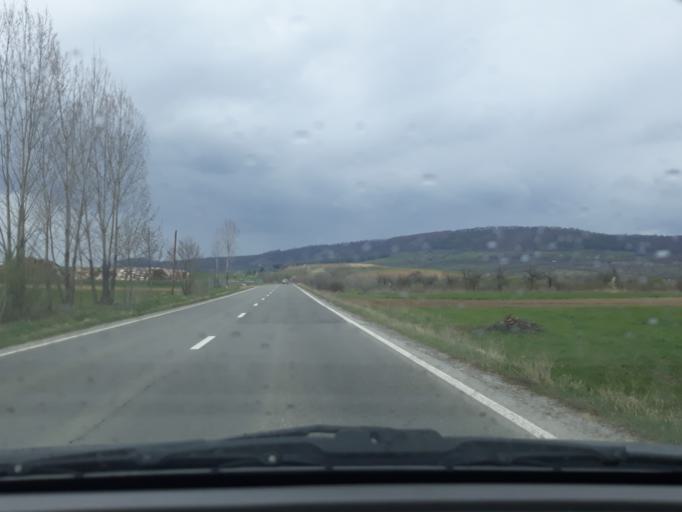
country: RO
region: Harghita
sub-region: Comuna Lupeni
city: Lupeni
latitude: 46.3889
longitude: 25.2162
